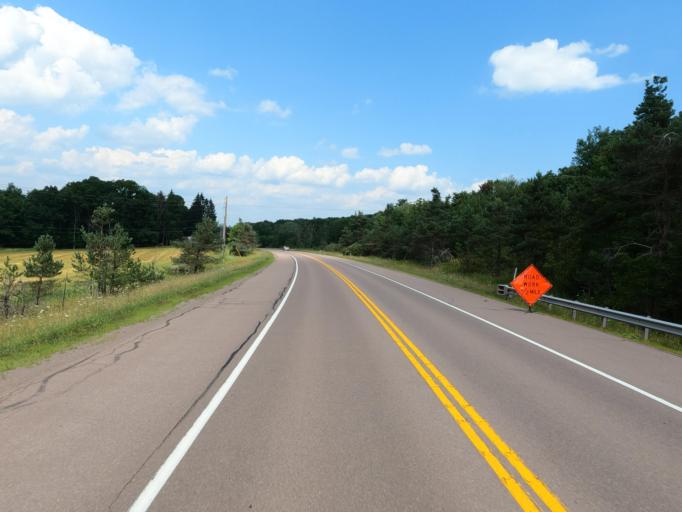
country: US
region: Maryland
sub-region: Garrett County
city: Oakland
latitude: 39.5807
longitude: -79.3620
